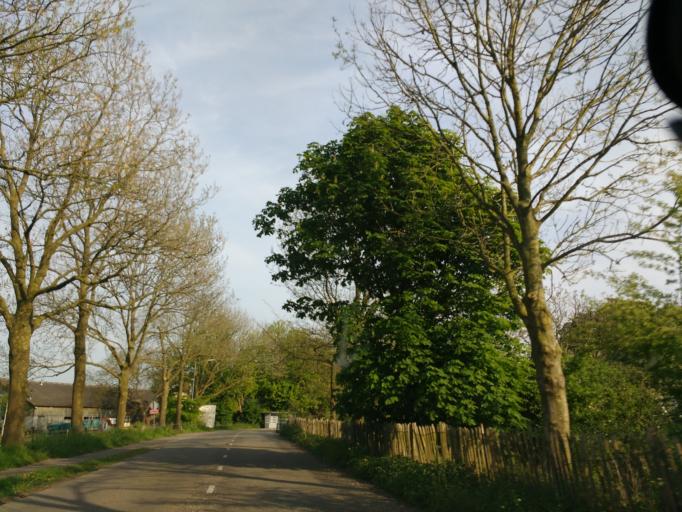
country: NL
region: Gelderland
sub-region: Gemeente Overbetuwe
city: Randwijk
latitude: 51.9622
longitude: 5.6887
